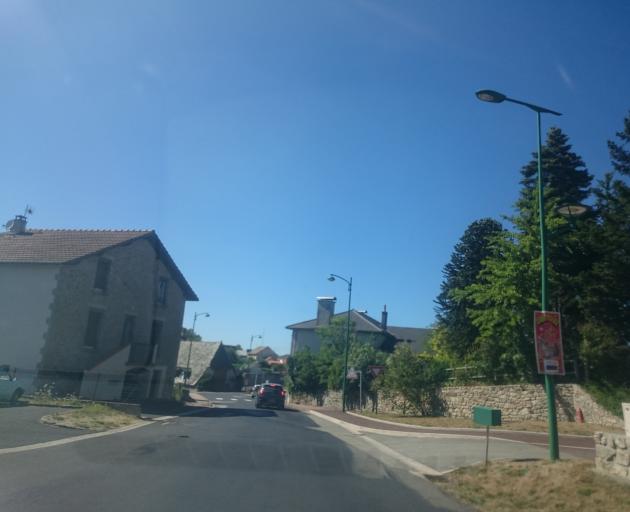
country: FR
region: Auvergne
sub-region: Departement du Cantal
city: Saint-Mamet-la-Salvetat
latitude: 44.8580
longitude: 2.3086
